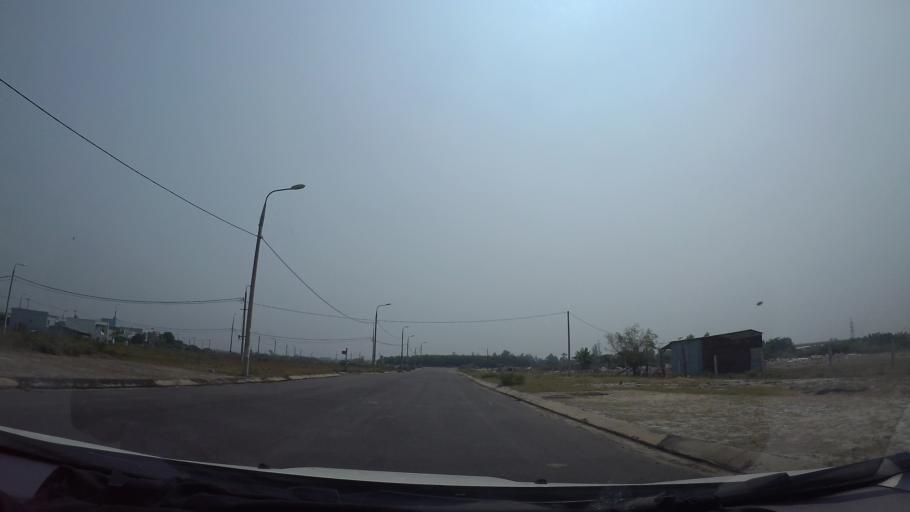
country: VN
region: Da Nang
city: Cam Le
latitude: 15.9739
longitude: 108.2137
